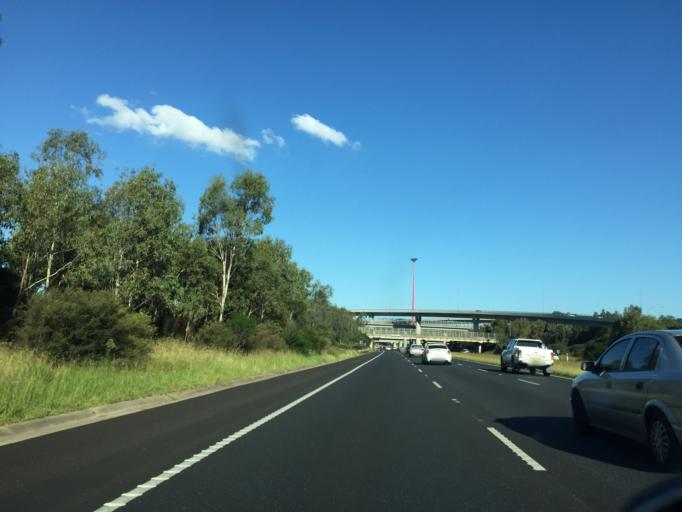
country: AU
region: New South Wales
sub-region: Blacktown
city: Doonside
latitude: -33.7968
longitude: 150.8504
